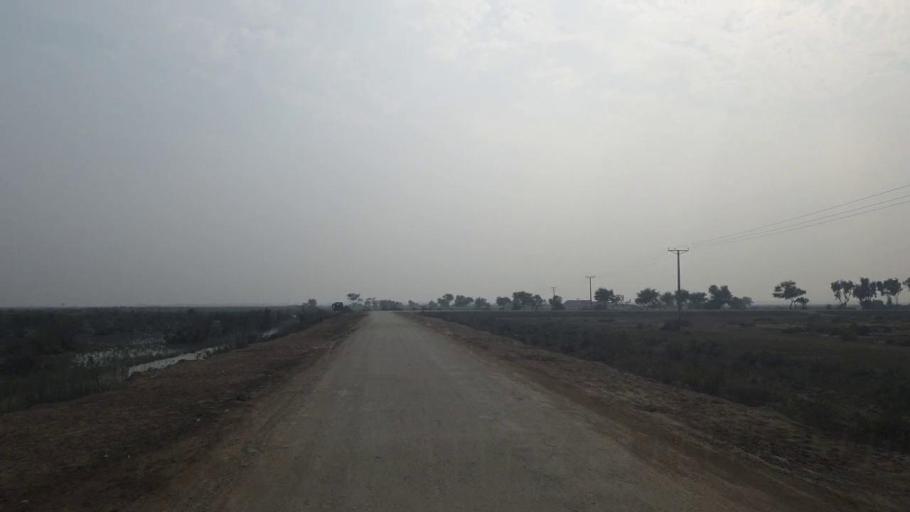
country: PK
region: Sindh
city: Tando Adam
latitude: 25.8243
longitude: 68.6967
